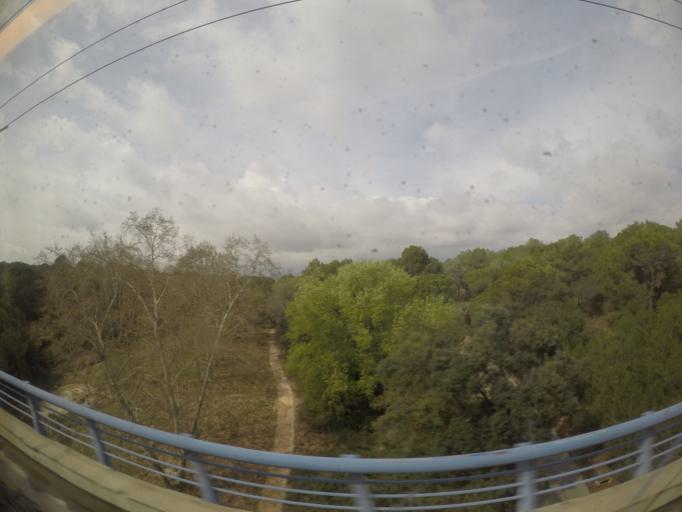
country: ES
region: Catalonia
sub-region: Provincia de Tarragona
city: Santa Oliva
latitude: 41.2586
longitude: 1.5823
